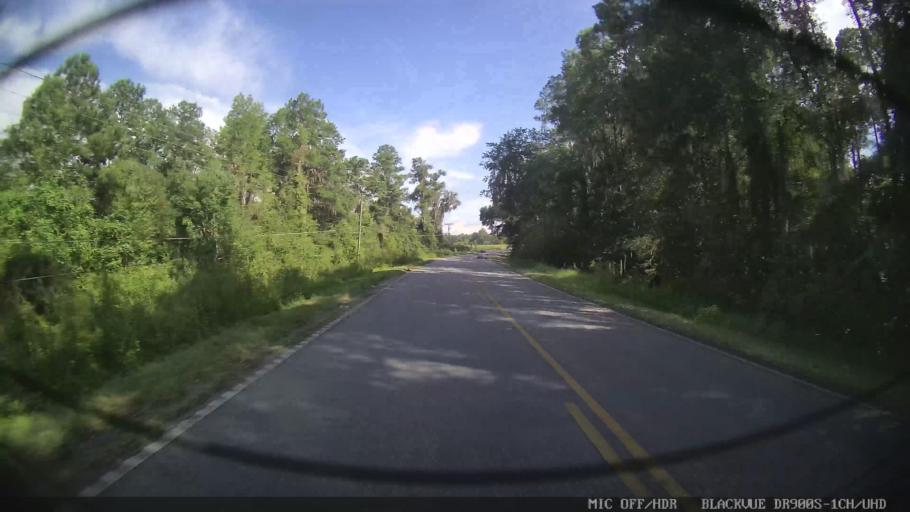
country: US
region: Georgia
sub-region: Lowndes County
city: Valdosta
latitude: 30.7189
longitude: -83.2435
